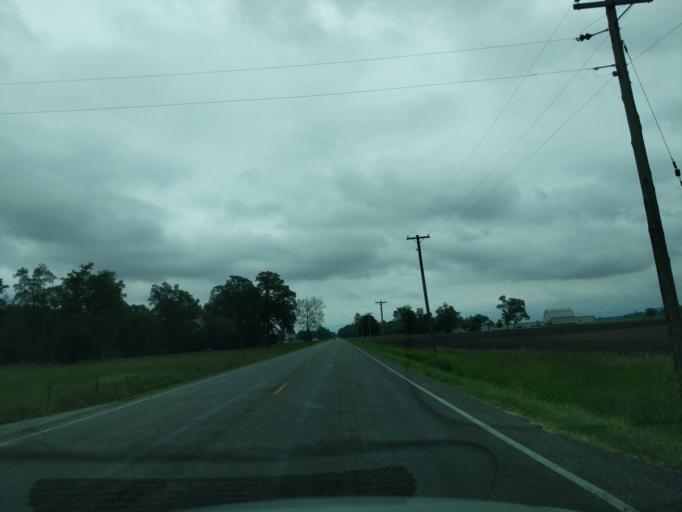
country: US
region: Indiana
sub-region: Tipton County
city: Tipton
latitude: 40.2833
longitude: -85.9798
